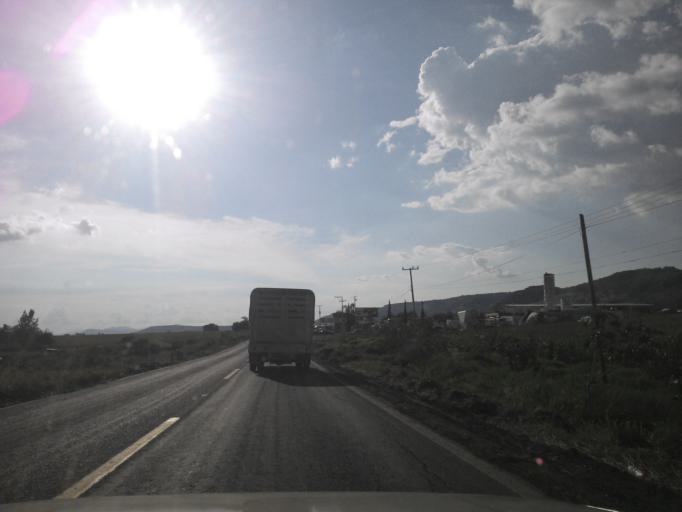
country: MX
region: Jalisco
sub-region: Atotonilco el Alto
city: San Francisco de Asis
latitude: 20.5421
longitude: -102.5848
